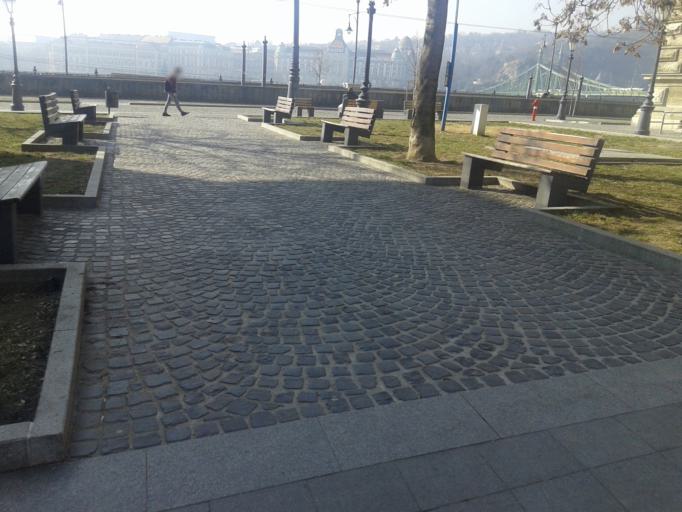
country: HU
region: Budapest
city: Budapest IX. keruelet
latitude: 47.4853
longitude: 19.0592
